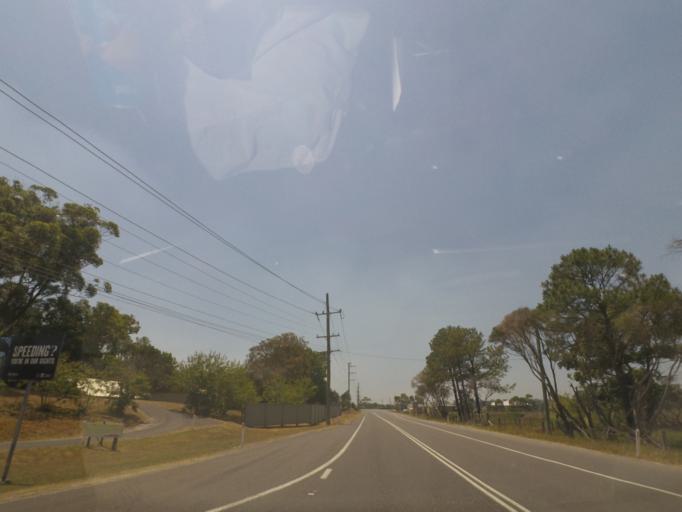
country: AU
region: New South Wales
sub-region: Port Stephens Shire
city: Medowie
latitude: -32.8030
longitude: 151.8828
